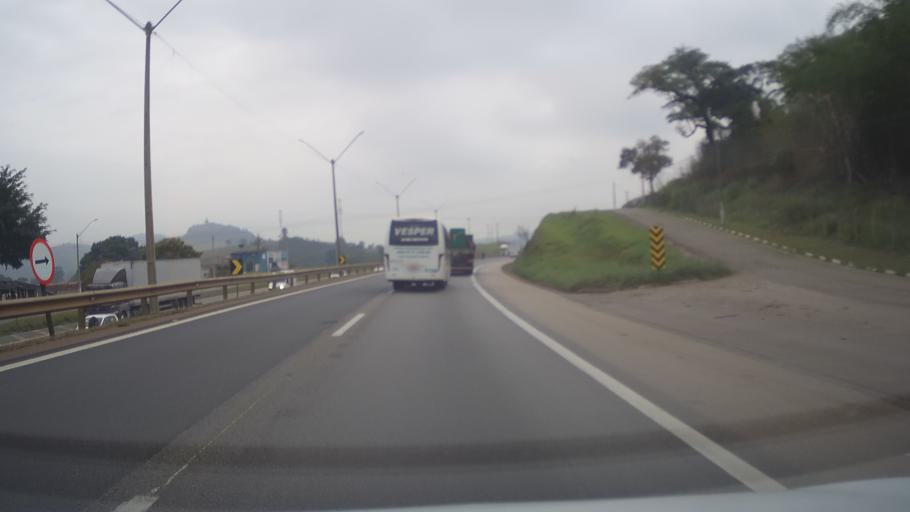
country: BR
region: Sao Paulo
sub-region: Atibaia
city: Atibaia
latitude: -23.0373
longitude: -46.5549
